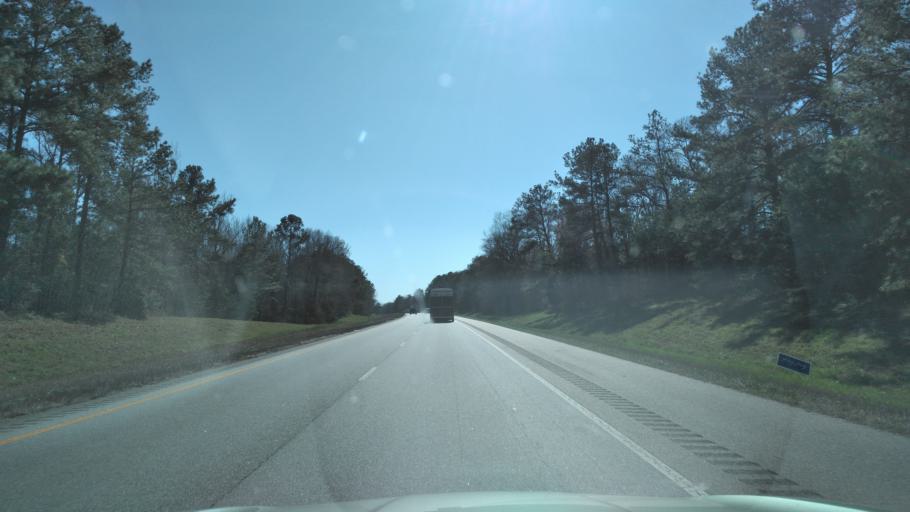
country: US
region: Alabama
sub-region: Lowndes County
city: Fort Deposit
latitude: 32.0529
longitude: -86.4985
